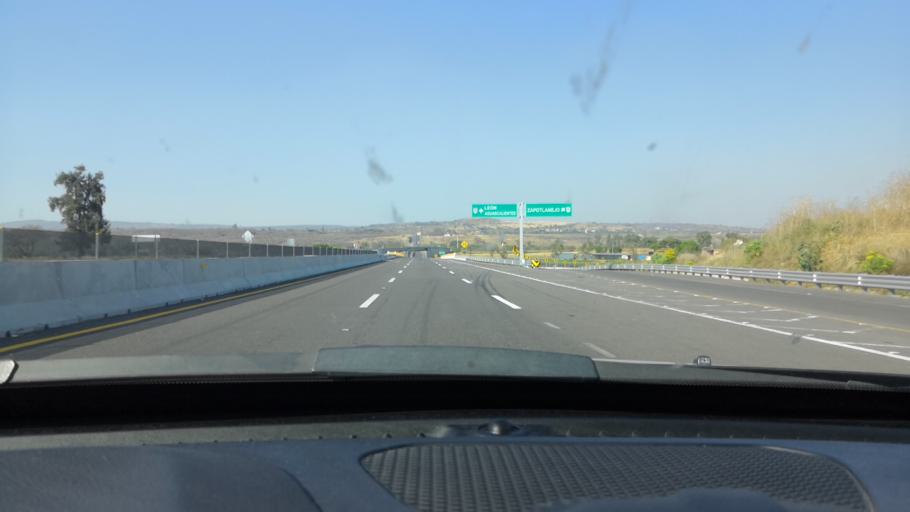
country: MX
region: Jalisco
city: Zapotlanejo
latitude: 20.6123
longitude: -103.1004
